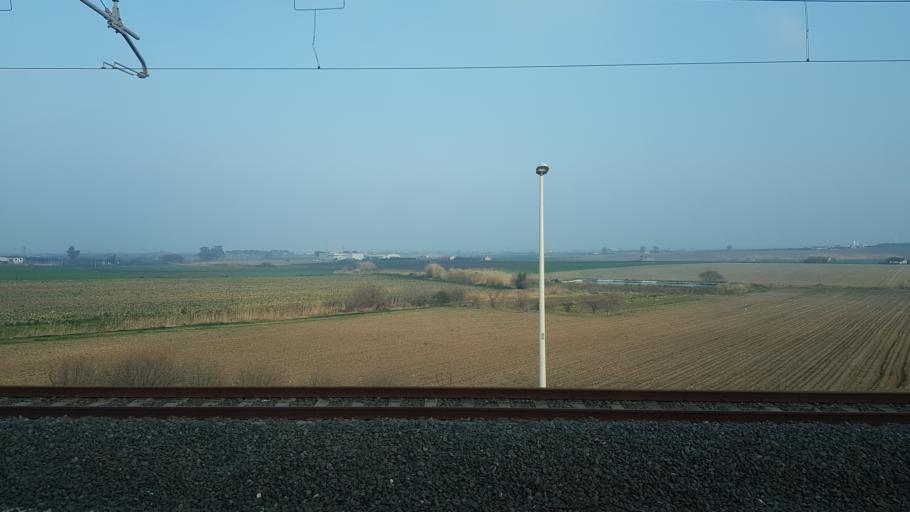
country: IT
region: Apulia
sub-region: Provincia di Foggia
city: Lesina
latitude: 41.8517
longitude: 15.2959
